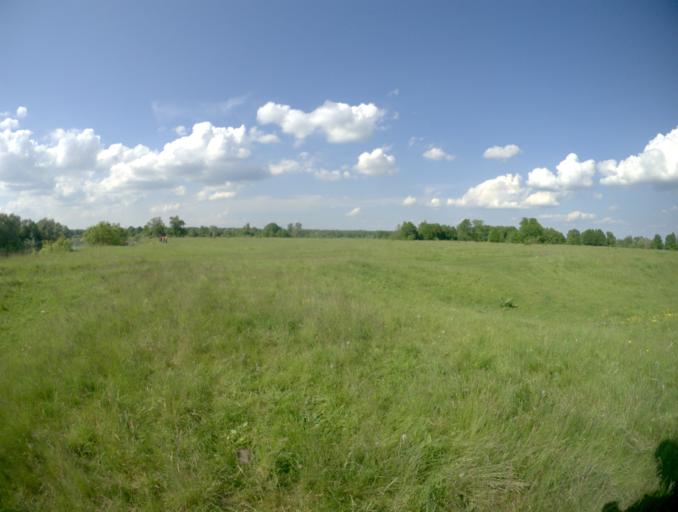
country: RU
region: Vladimir
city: Raduzhnyy
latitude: 56.0412
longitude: 40.3009
